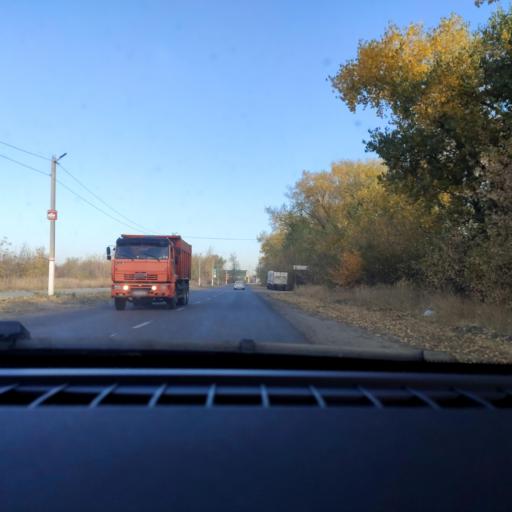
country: RU
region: Voronezj
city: Somovo
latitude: 51.6734
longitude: 39.3229
